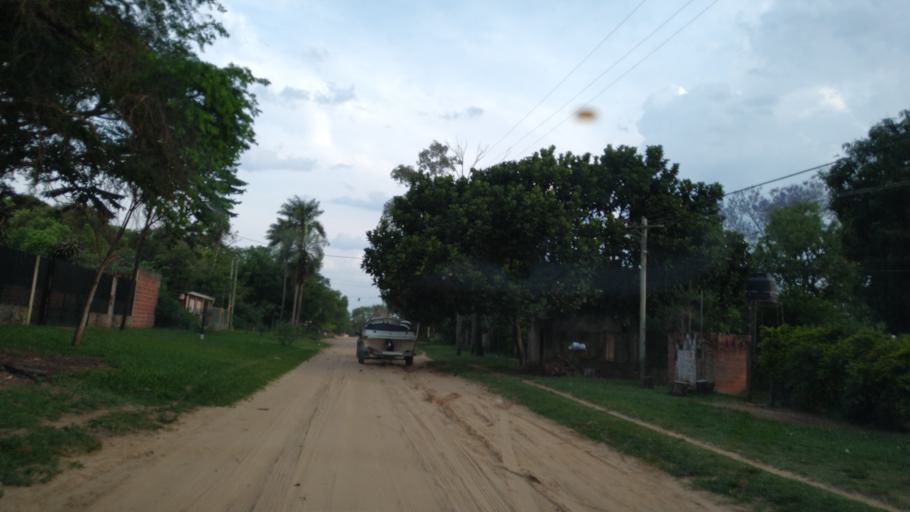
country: AR
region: Corrientes
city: Ituzaingo
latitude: -27.5928
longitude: -56.7047
